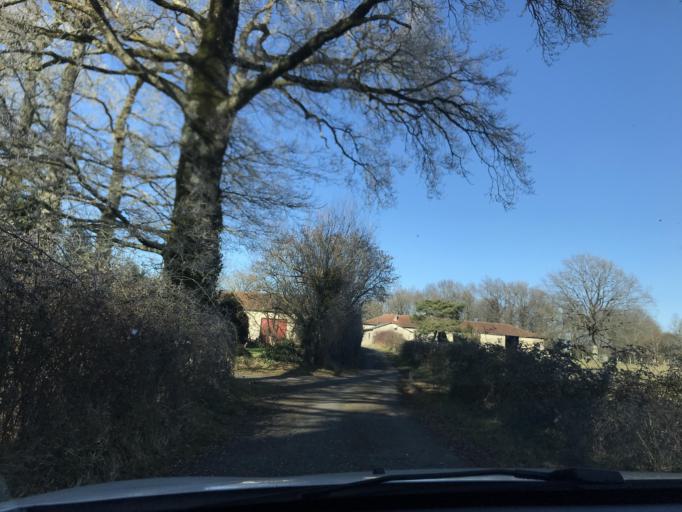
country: FR
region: Poitou-Charentes
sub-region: Departement de la Charente
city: Saint-Claud
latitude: 45.8505
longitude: 0.5268
